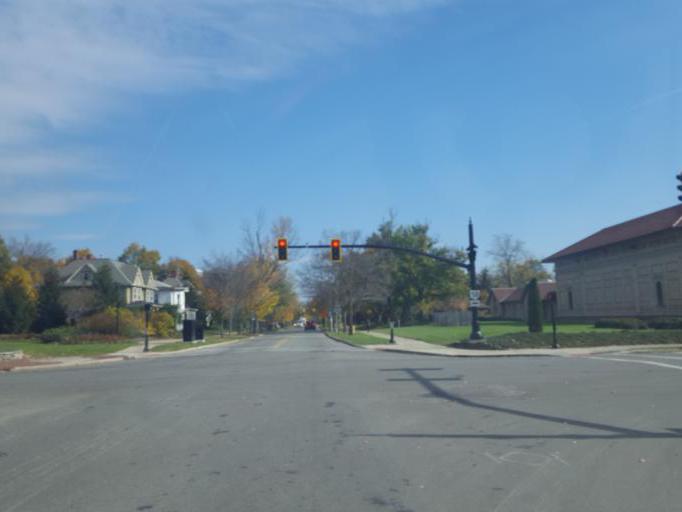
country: US
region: Ohio
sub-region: Lorain County
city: Oberlin
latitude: 41.2941
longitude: -82.2176
